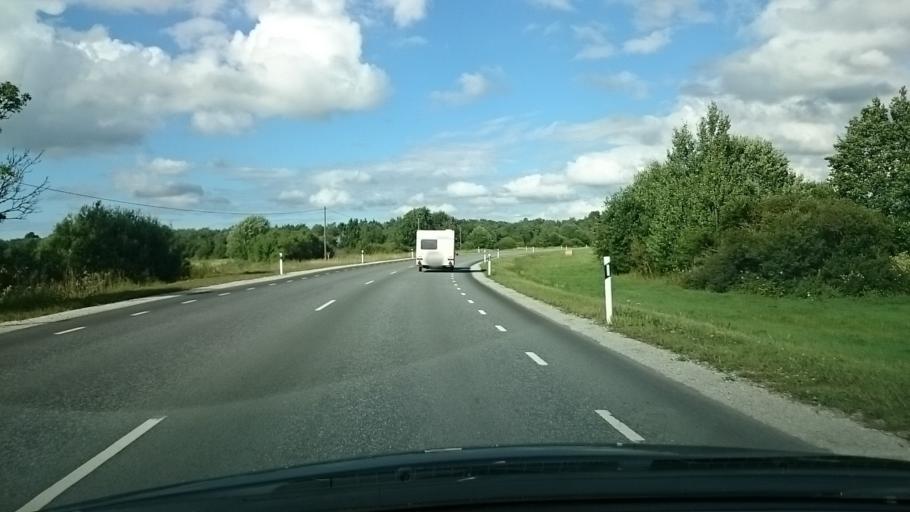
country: EE
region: Harju
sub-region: Keila linn
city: Keila
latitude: 59.2975
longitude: 24.3453
